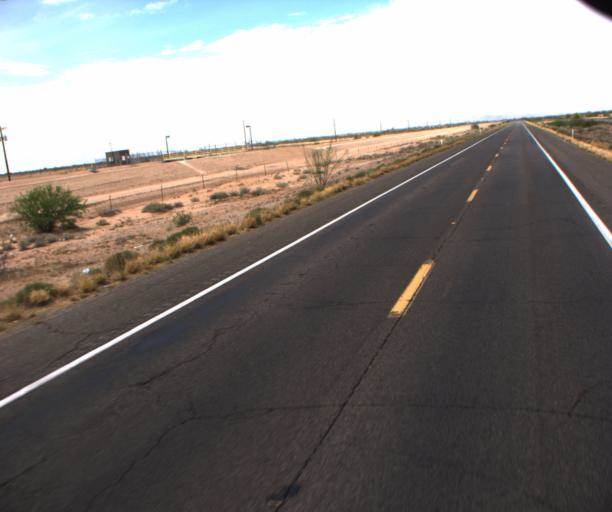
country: US
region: Arizona
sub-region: Maricopa County
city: Sun Lakes
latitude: 33.1829
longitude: -111.8081
